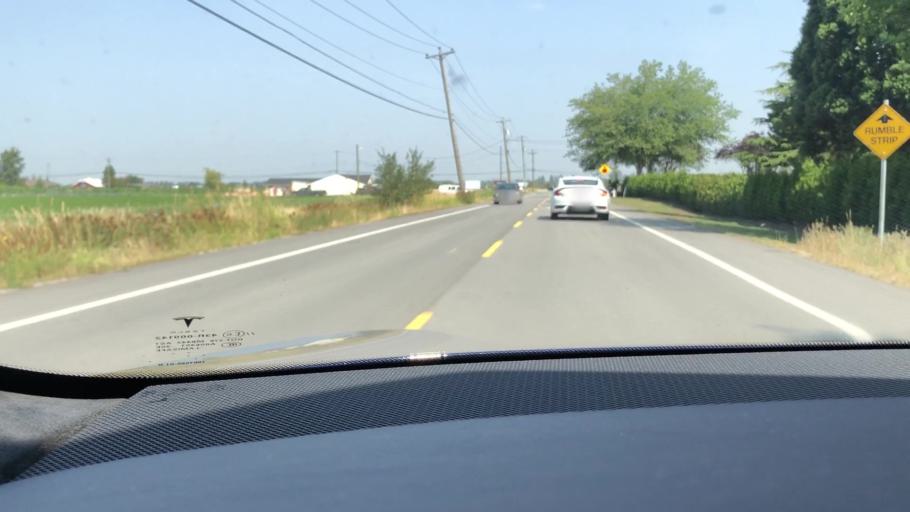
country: CA
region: British Columbia
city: Ladner
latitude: 49.0519
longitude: -123.0798
